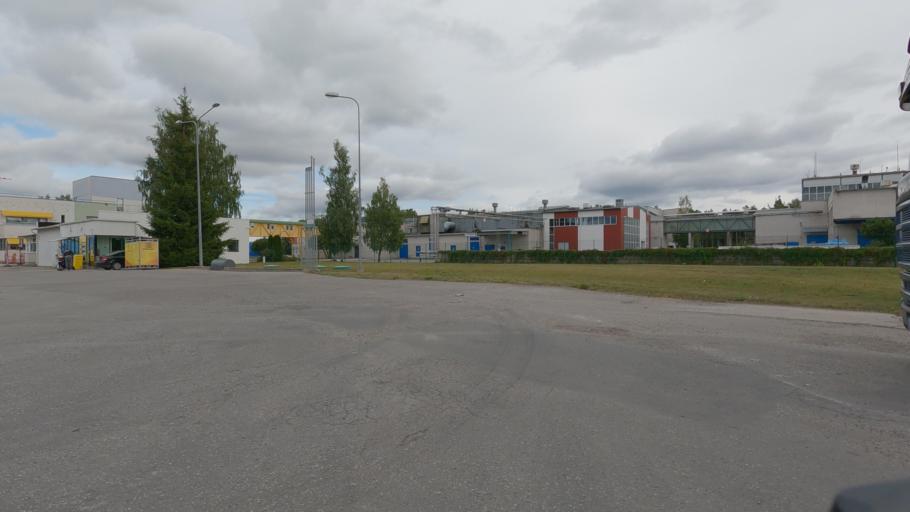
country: EE
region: Raplamaa
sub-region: Rapla vald
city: Rapla
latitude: 58.9934
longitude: 24.7947
